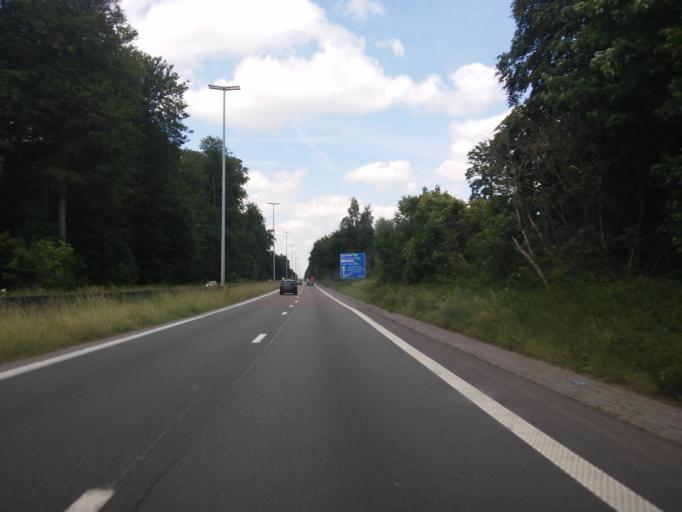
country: BE
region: Flanders
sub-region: Provincie Vlaams-Brabant
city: Hoeilaart
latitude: 50.7876
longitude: 4.4564
